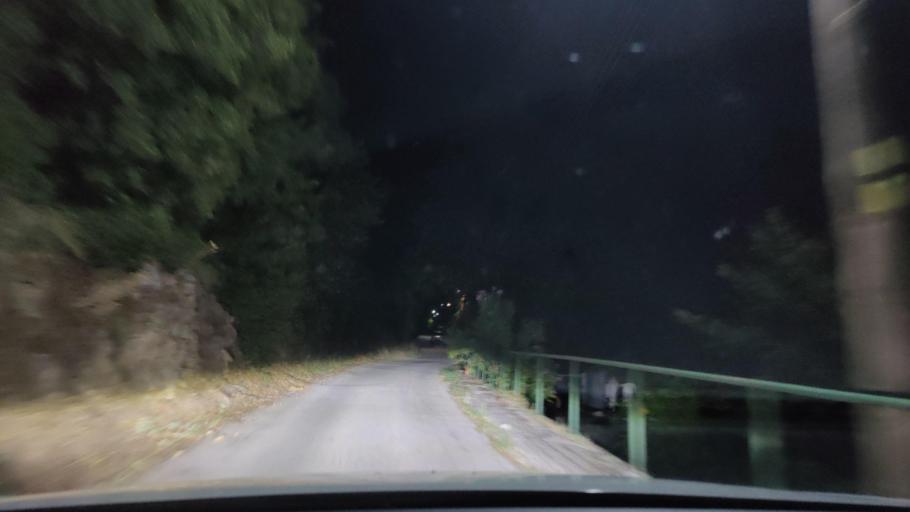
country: GR
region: Central Macedonia
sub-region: Nomos Serron
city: Neo Petritsi
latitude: 41.2791
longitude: 23.2908
